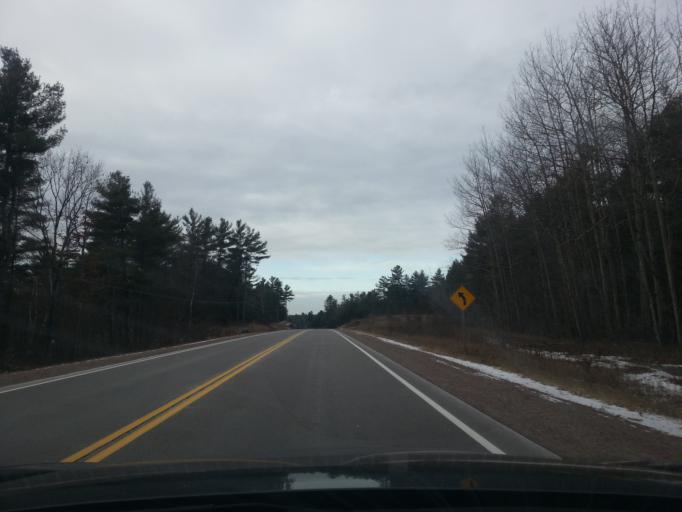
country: CA
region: Ontario
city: Deseronto
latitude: 44.5612
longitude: -77.2425
